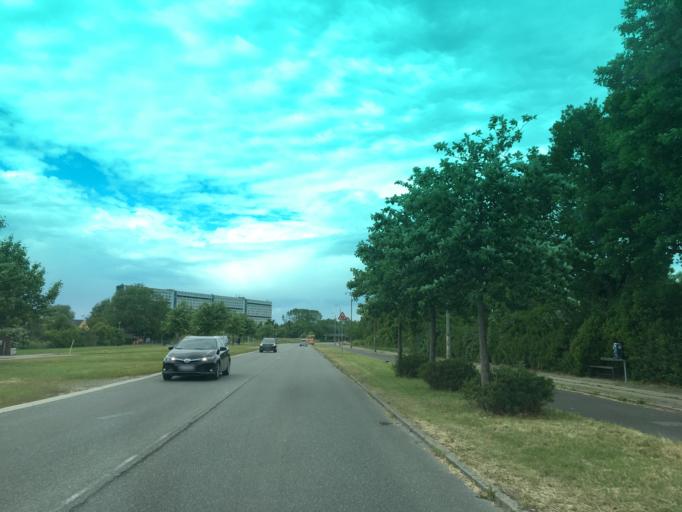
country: DK
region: Capital Region
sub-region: Hvidovre Kommune
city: Hvidovre
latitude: 55.6224
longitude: 12.4596
